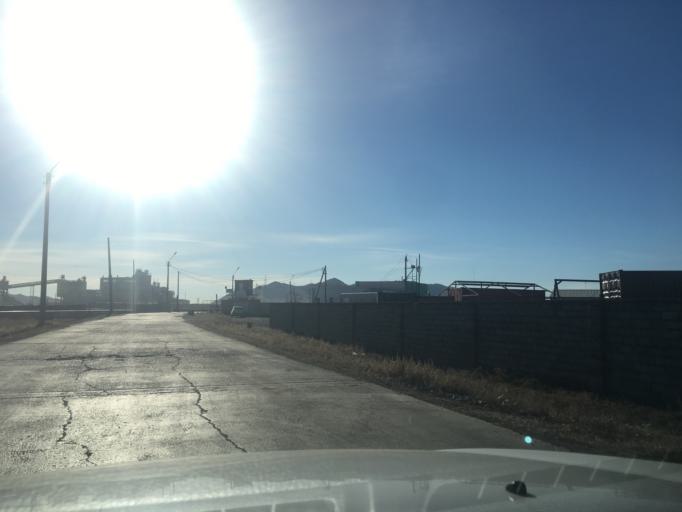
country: MN
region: Ulaanbaatar
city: Ulaanbaatar
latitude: 47.8985
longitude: 106.7346
